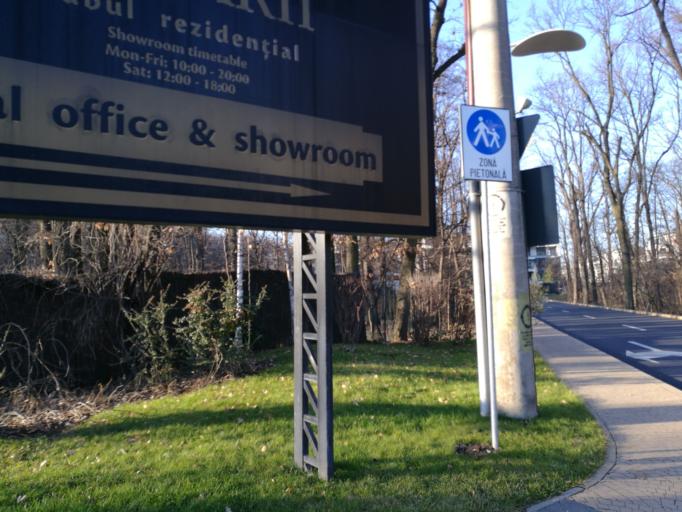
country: RO
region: Ilfov
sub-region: Comuna Otopeni
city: Otopeni
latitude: 44.5120
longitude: 26.0726
